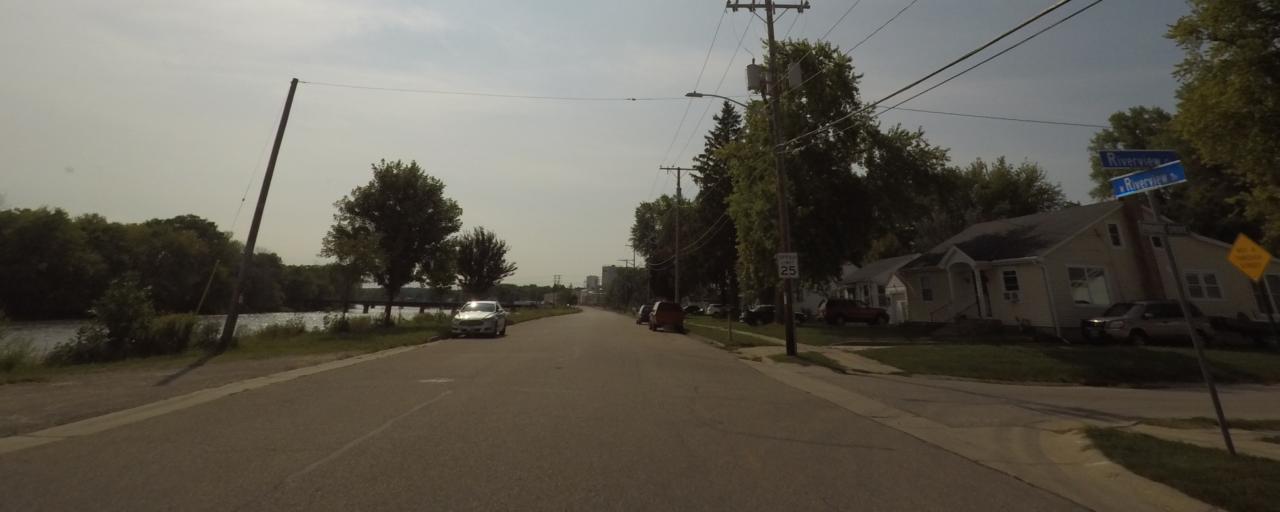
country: US
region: Wisconsin
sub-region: Jefferson County
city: Jefferson
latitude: 43.0001
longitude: -88.8122
